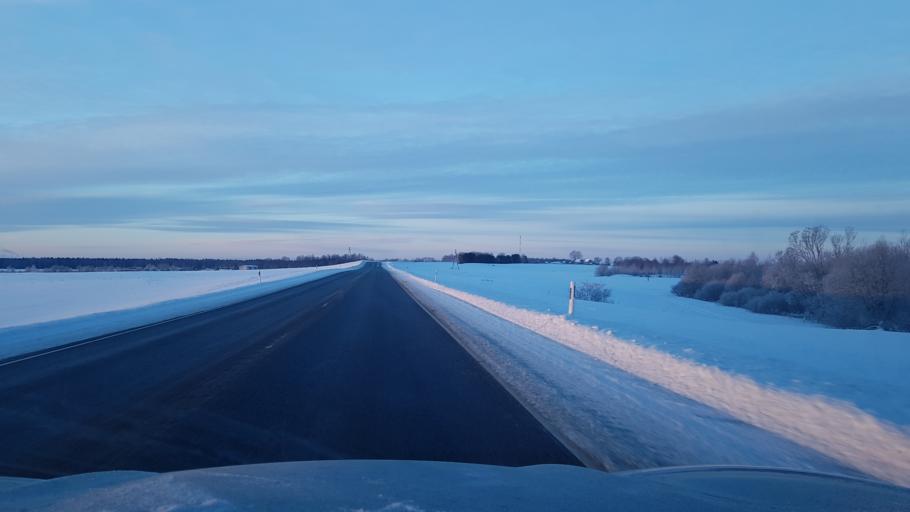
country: EE
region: Ida-Virumaa
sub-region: Narva-Joesuu linn
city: Narva-Joesuu
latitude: 59.3944
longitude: 27.9957
